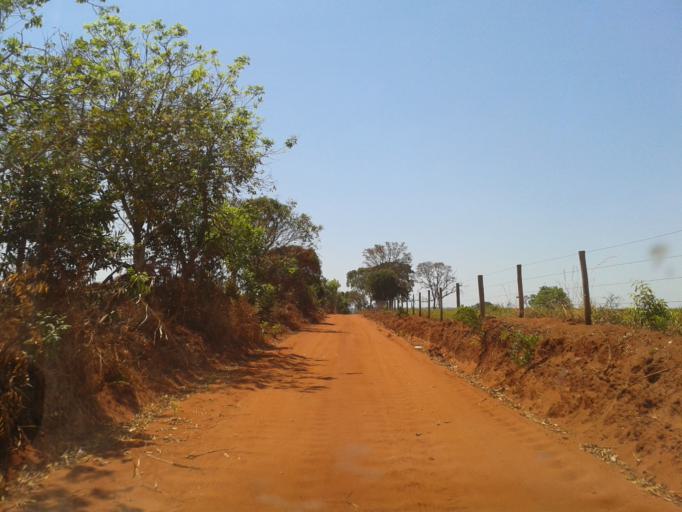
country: BR
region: Minas Gerais
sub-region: Ituiutaba
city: Ituiutaba
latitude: -19.0719
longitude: -49.3302
